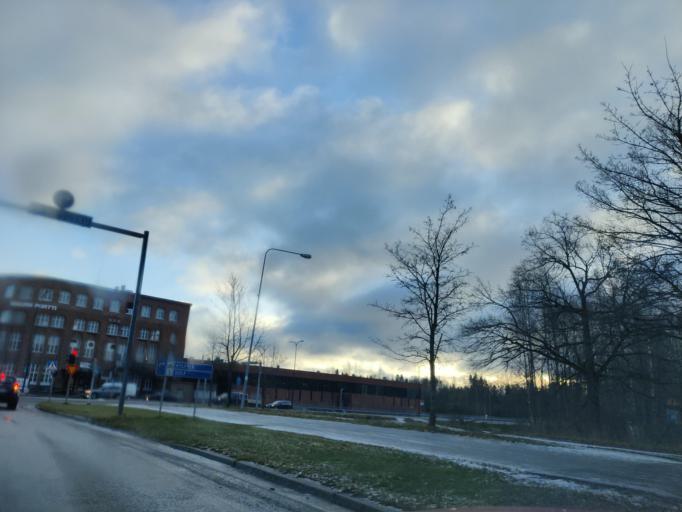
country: FI
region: Pirkanmaa
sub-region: Tampere
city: Nokia
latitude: 61.4747
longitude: 23.5044
